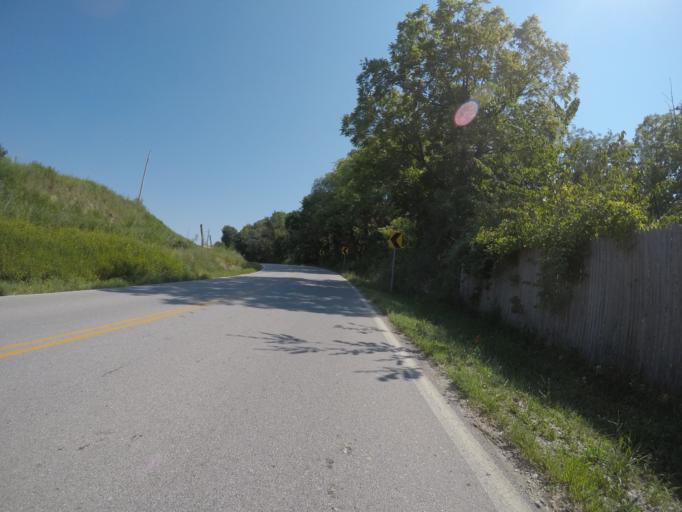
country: US
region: Kansas
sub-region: Leavenworth County
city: Lansing
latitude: 39.2125
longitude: -94.8398
